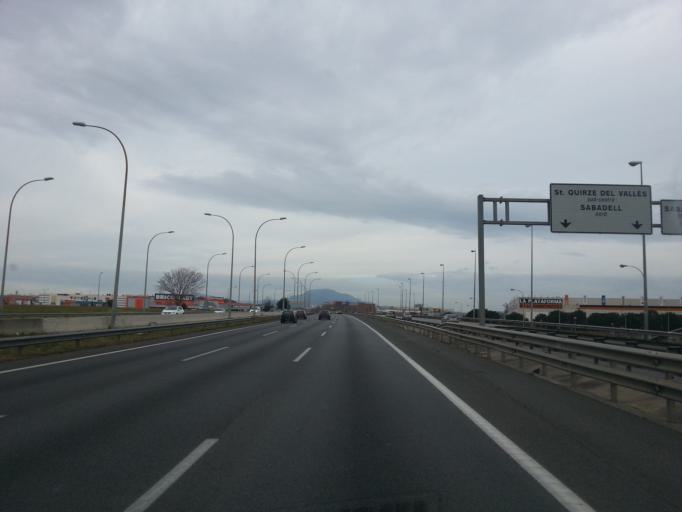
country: ES
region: Catalonia
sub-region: Provincia de Barcelona
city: Sant Quirze del Valles
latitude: 41.5280
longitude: 2.0946
